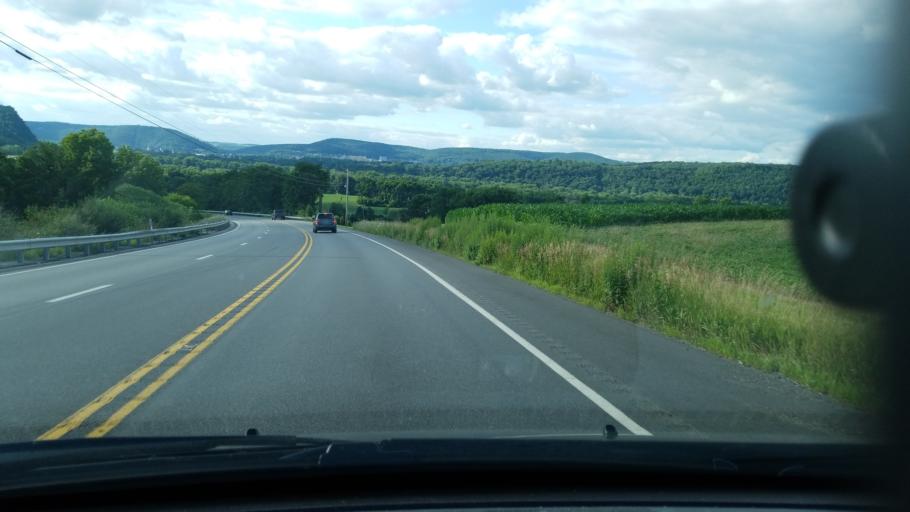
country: US
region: Pennsylvania
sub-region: Montour County
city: Mechanicsville
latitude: 40.9270
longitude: -76.5885
